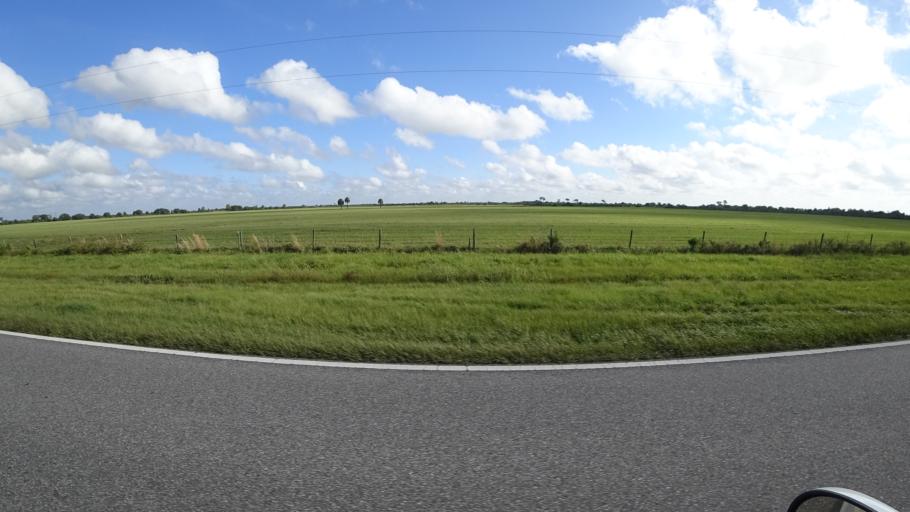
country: US
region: Florida
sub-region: Hillsborough County
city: Wimauma
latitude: 27.5230
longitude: -82.3310
